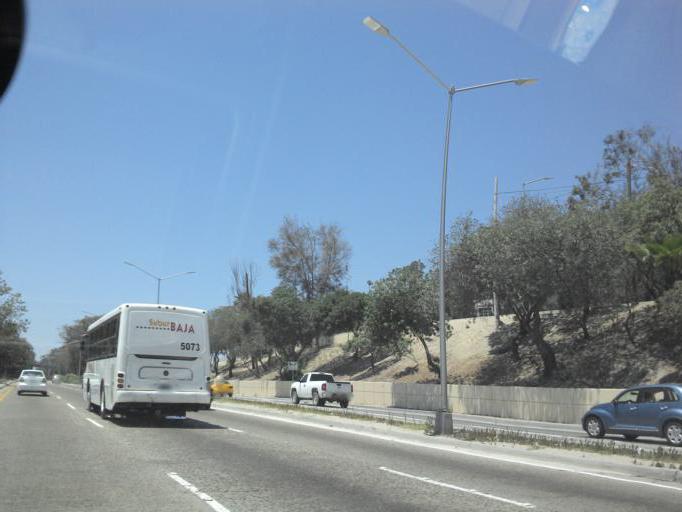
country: MX
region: Baja California
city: Tijuana
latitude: 32.5196
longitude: -117.0018
